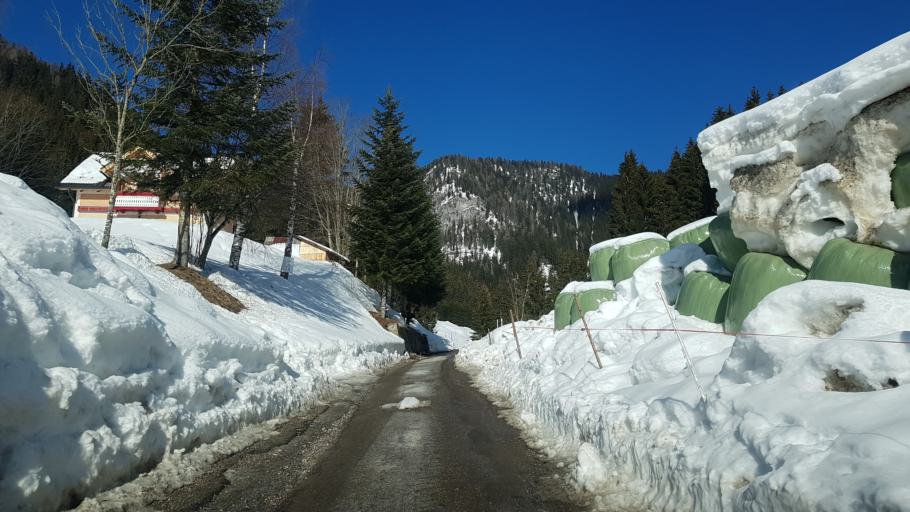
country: IT
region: Friuli Venezia Giulia
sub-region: Provincia di Udine
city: Malborghetto
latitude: 46.5475
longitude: 13.4783
